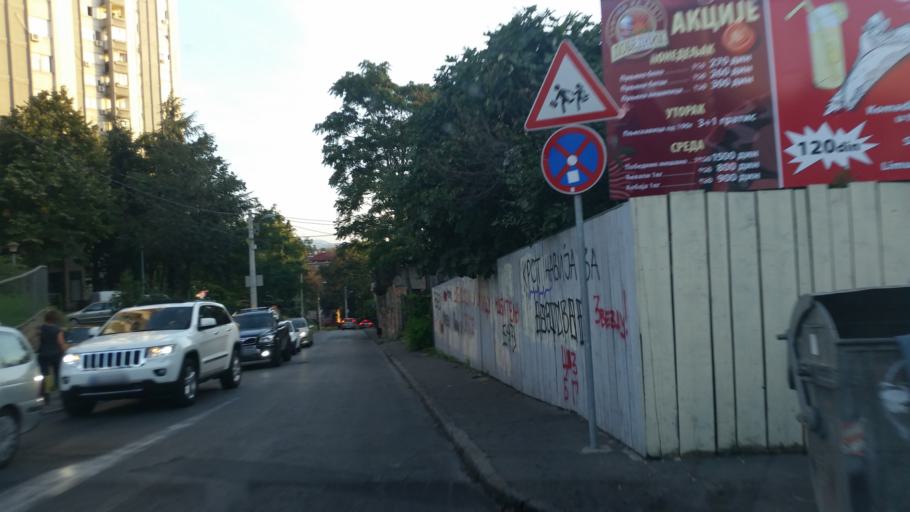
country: RS
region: Central Serbia
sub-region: Belgrade
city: Vracar
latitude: 44.7953
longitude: 20.4899
